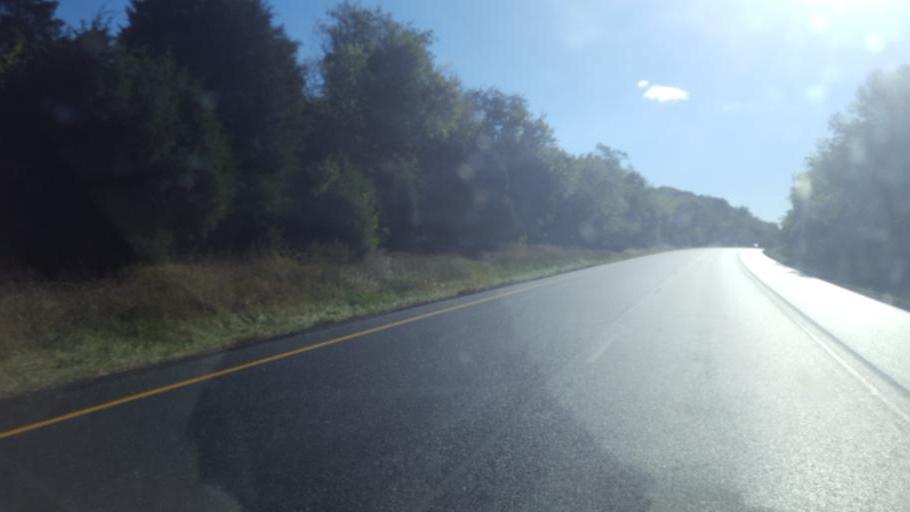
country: US
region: Maryland
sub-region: Washington County
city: Wilson-Conococheague
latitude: 39.6497
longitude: -77.8493
